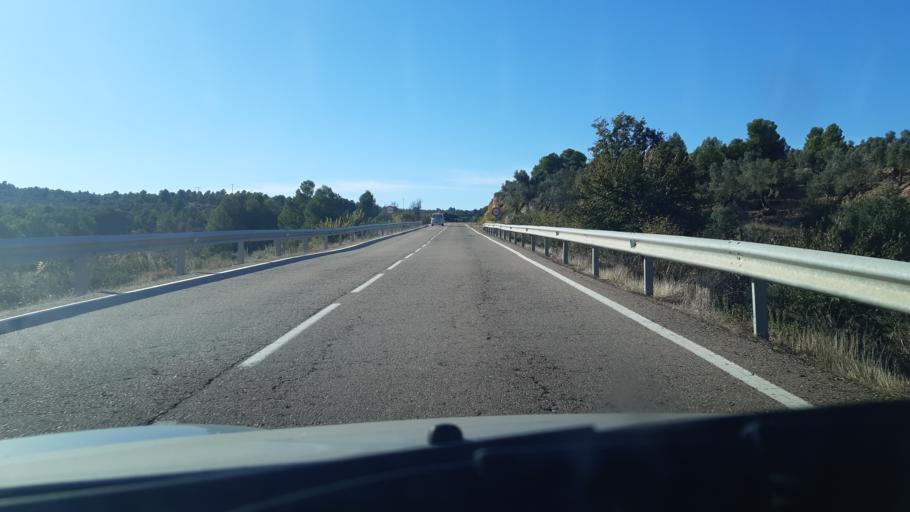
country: ES
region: Aragon
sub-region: Provincia de Teruel
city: Valjunquera
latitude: 40.9554
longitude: 0.0072
